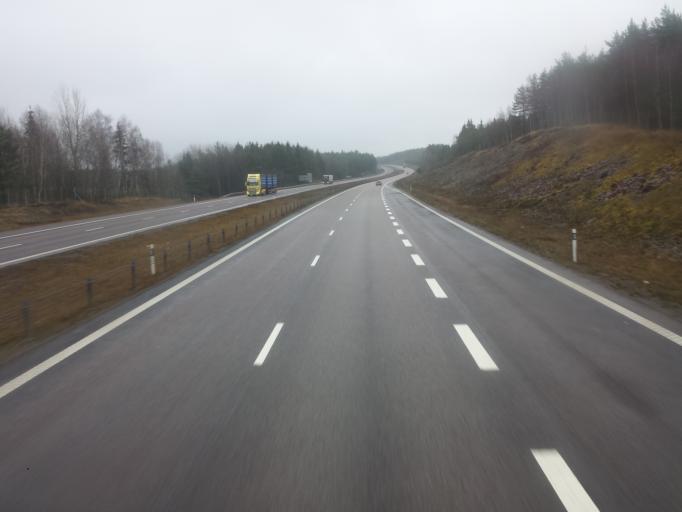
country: SE
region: Soedermanland
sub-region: Nykopings Kommun
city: Olstorp
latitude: 58.7562
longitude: 16.6256
